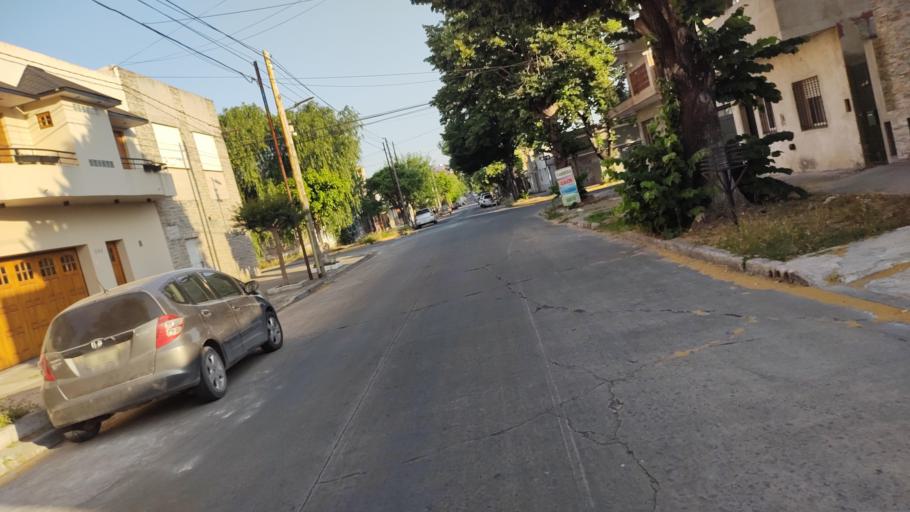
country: AR
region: Buenos Aires
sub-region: Partido de La Plata
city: La Plata
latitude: -34.9309
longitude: -57.9740
